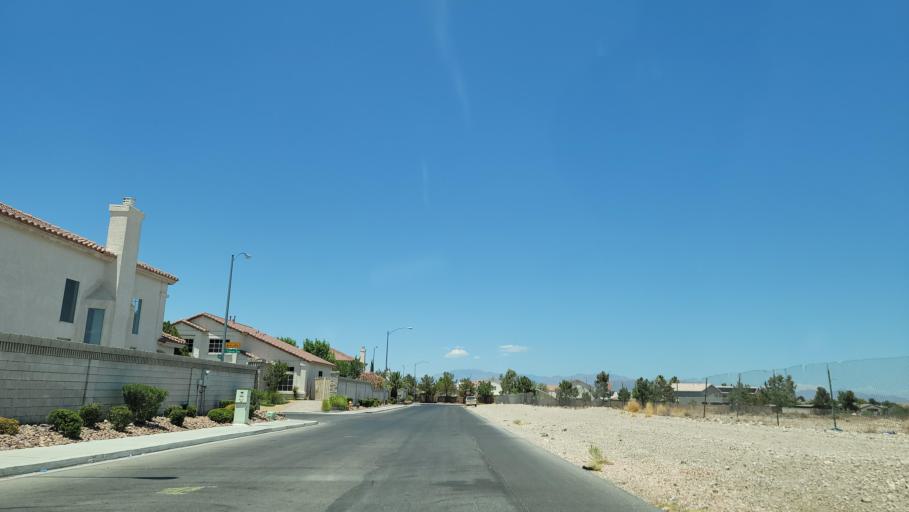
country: US
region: Nevada
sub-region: Clark County
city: Spring Valley
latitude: 36.0798
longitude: -115.2724
